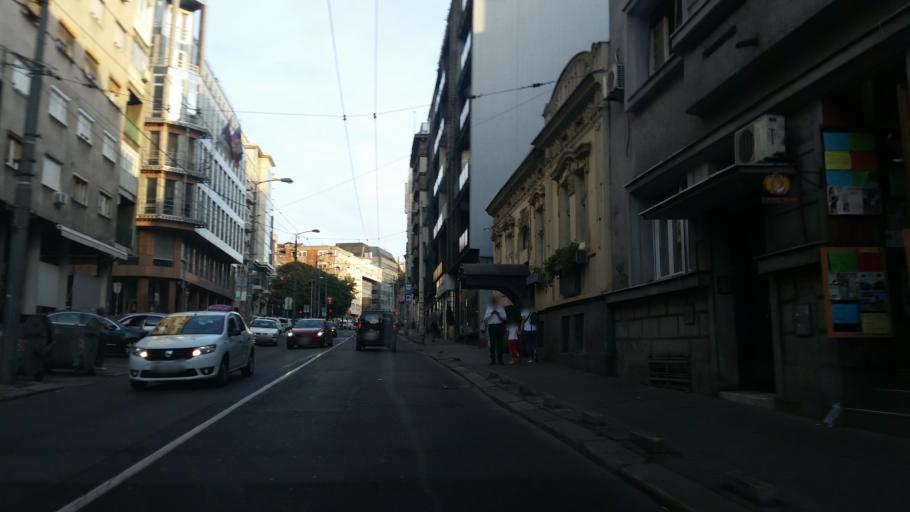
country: RS
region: Central Serbia
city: Belgrade
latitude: 44.8017
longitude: 20.4685
